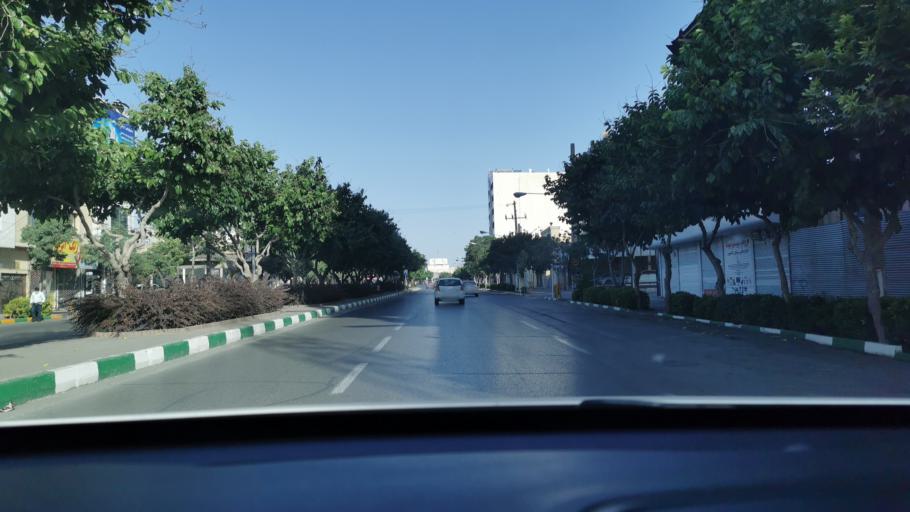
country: IR
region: Razavi Khorasan
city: Mashhad
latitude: 36.3324
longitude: 59.5160
